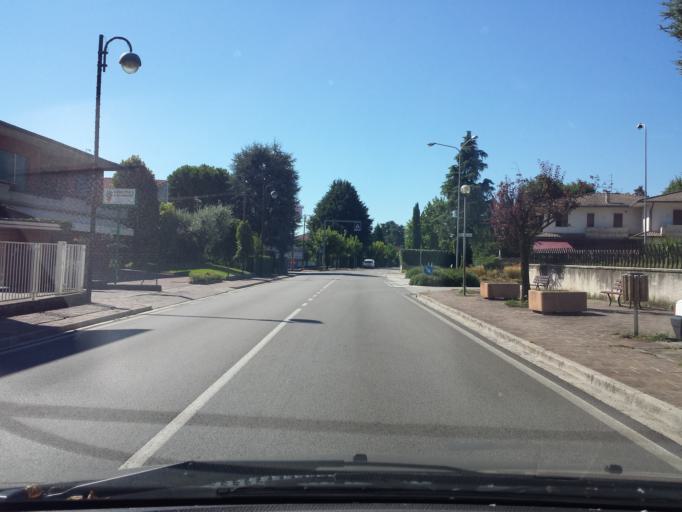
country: IT
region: Veneto
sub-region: Provincia di Vicenza
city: Breganze
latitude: 45.7028
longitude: 11.5648
